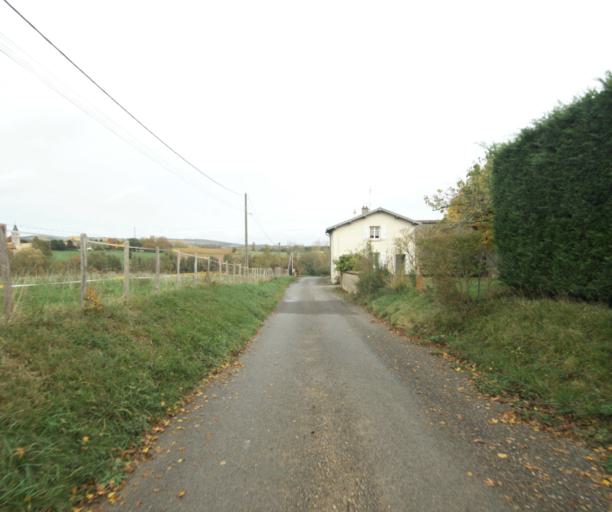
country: FR
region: Rhone-Alpes
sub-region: Departement de l'Ain
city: Pont-de-Vaux
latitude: 46.4726
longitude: 4.8745
